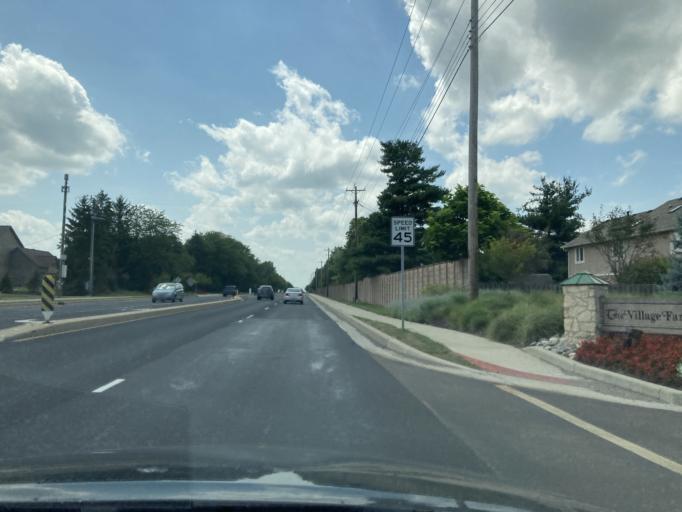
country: US
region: Indiana
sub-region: Hamilton County
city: Carmel
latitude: 39.9997
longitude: -86.1544
